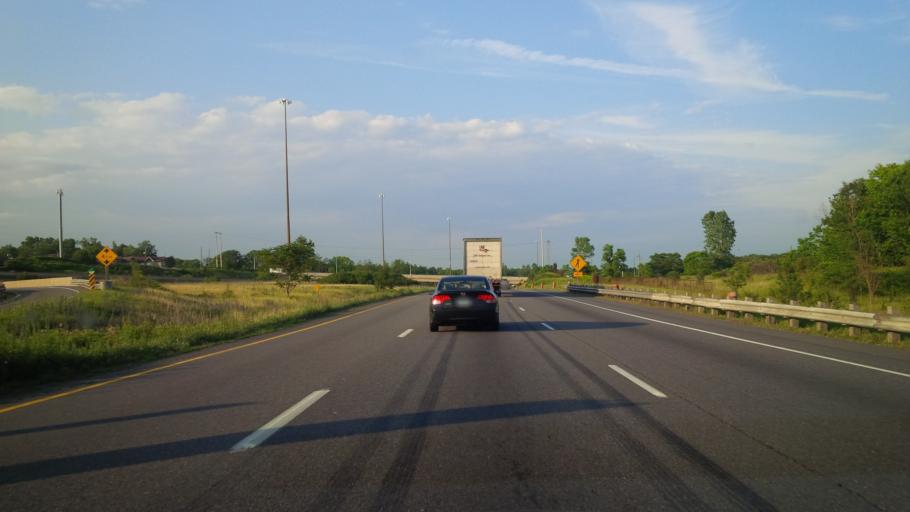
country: CA
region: Ontario
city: Hamilton
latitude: 43.2920
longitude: -79.8935
